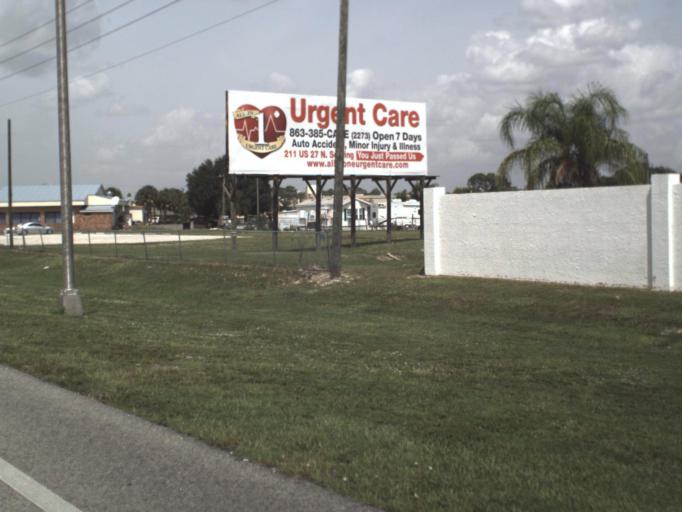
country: US
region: Florida
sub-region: Highlands County
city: Sebring
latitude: 27.4941
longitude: -81.4859
